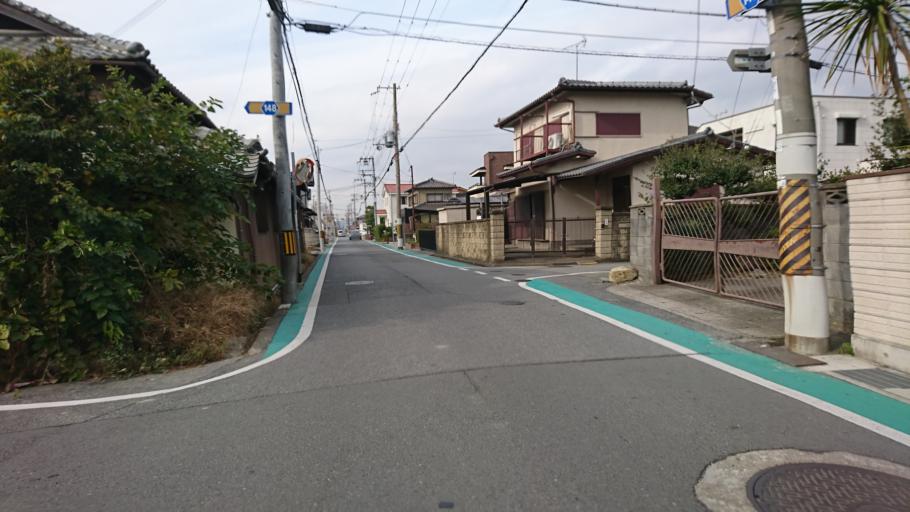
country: JP
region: Hyogo
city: Kakogawacho-honmachi
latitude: 34.7684
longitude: 134.8530
